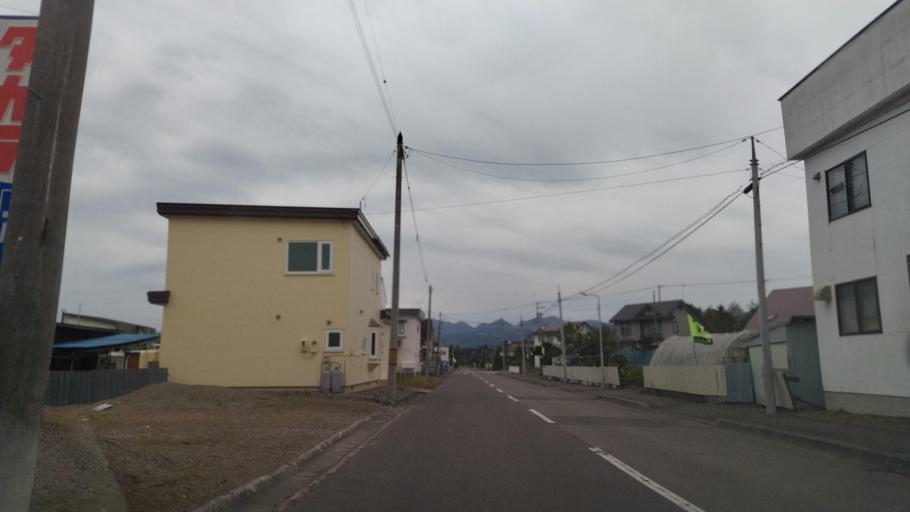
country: JP
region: Hokkaido
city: Otofuke
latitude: 43.2310
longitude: 143.2857
